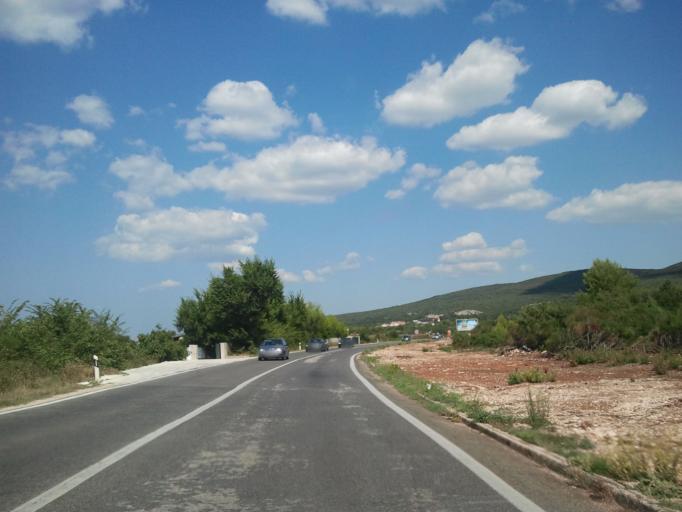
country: HR
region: Zadarska
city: Turanj
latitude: 43.9791
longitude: 15.3947
